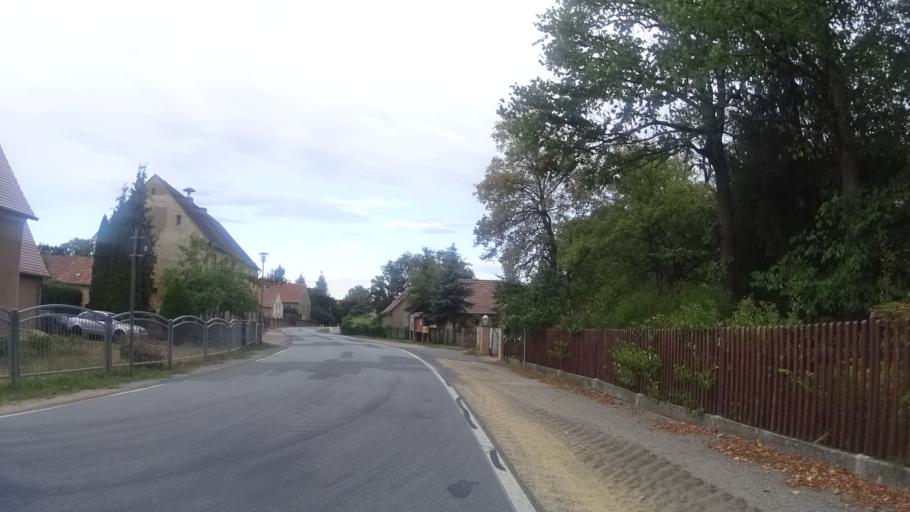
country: DE
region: Saxony
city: Rothenburg
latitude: 51.3120
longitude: 14.9985
